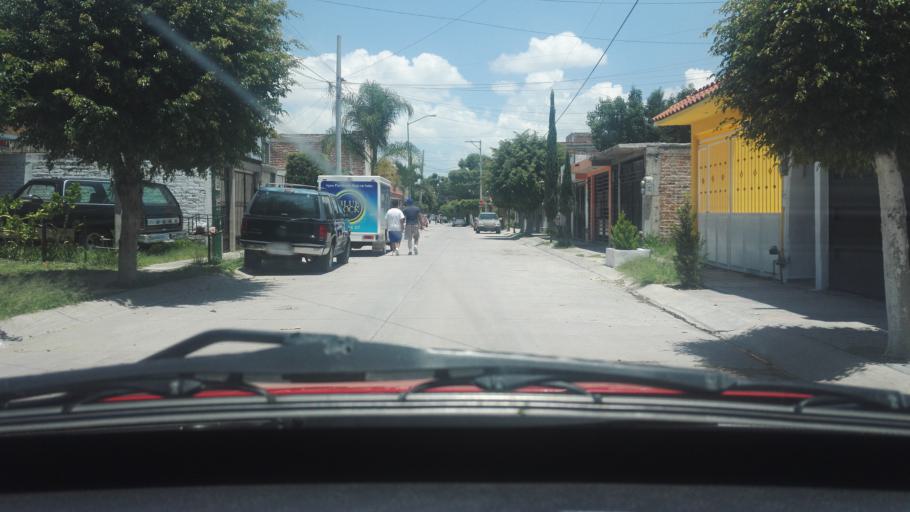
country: MX
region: Guanajuato
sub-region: Leon
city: San Jose de Duran (Los Troncoso)
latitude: 21.0785
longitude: -101.6398
